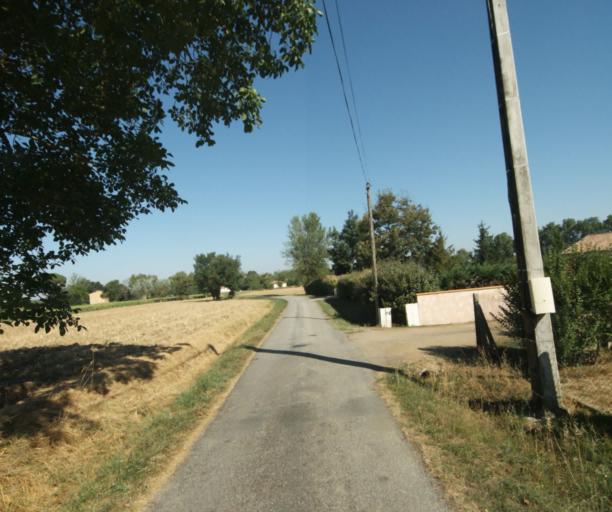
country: FR
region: Midi-Pyrenees
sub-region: Departement de la Haute-Garonne
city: Revel
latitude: 43.4676
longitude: 1.9584
